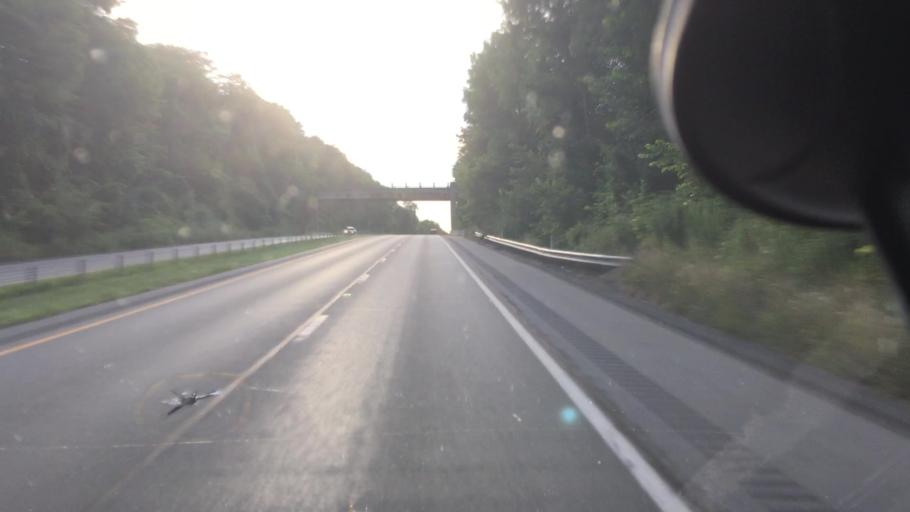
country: US
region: Pennsylvania
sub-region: Beaver County
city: Big Beaver
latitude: 40.7961
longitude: -80.4250
